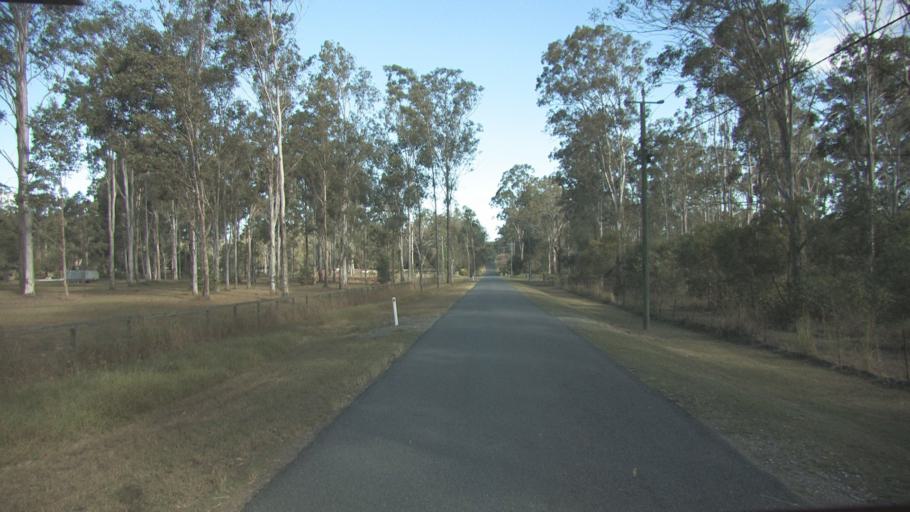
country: AU
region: Queensland
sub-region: Logan
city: North Maclean
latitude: -27.8234
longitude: 153.0630
